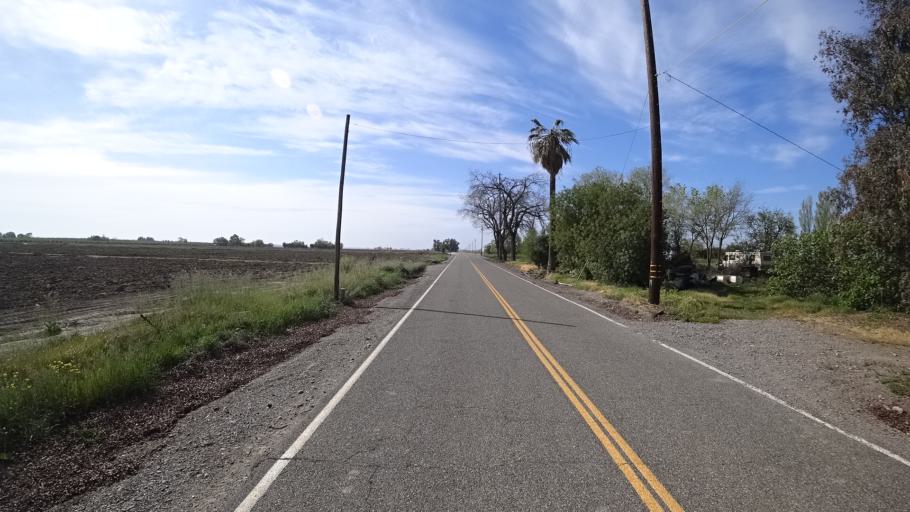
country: US
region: California
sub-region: Glenn County
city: Hamilton City
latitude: 39.6284
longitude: -122.0367
